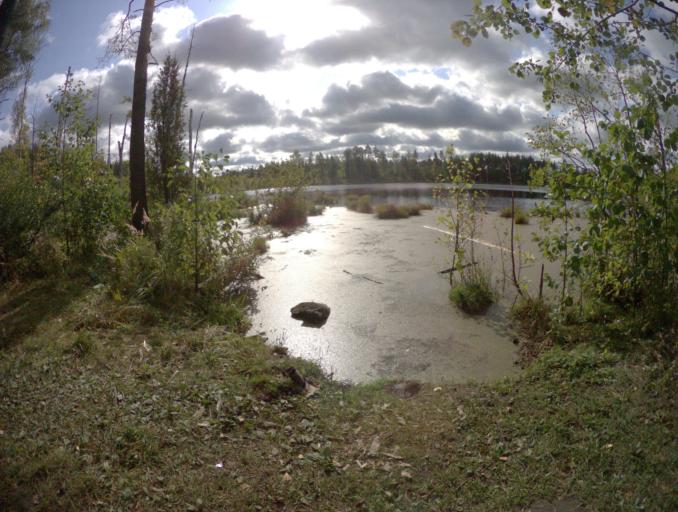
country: RU
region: Moskovskaya
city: Baksheyevo
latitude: 55.7366
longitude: 39.8225
